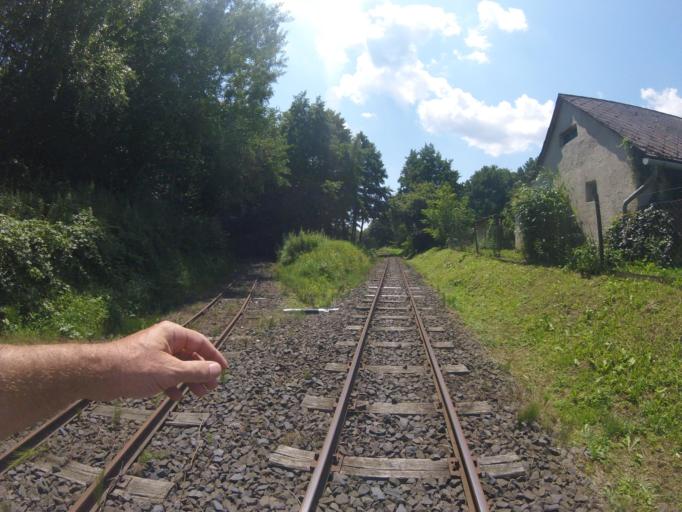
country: HU
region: Zala
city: Letenye
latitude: 46.5158
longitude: 16.7280
